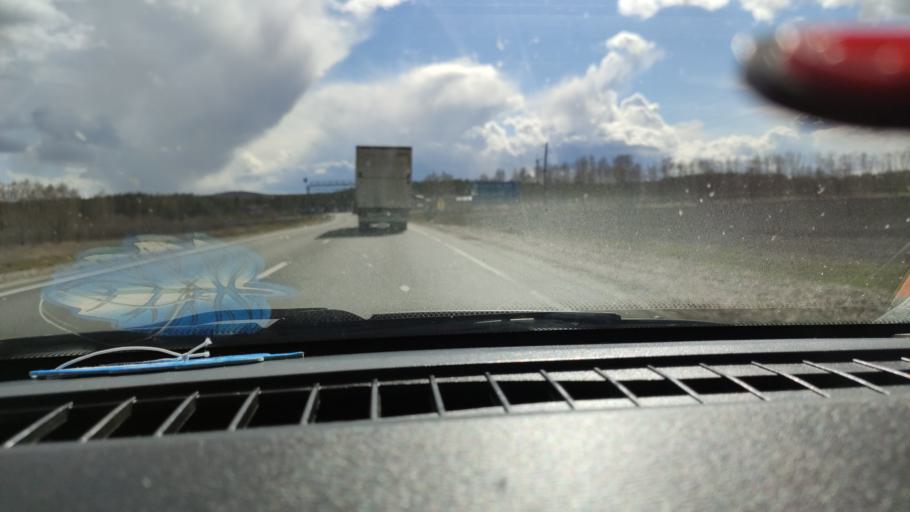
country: RU
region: Saratov
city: Khvalynsk
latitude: 52.5238
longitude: 48.0214
